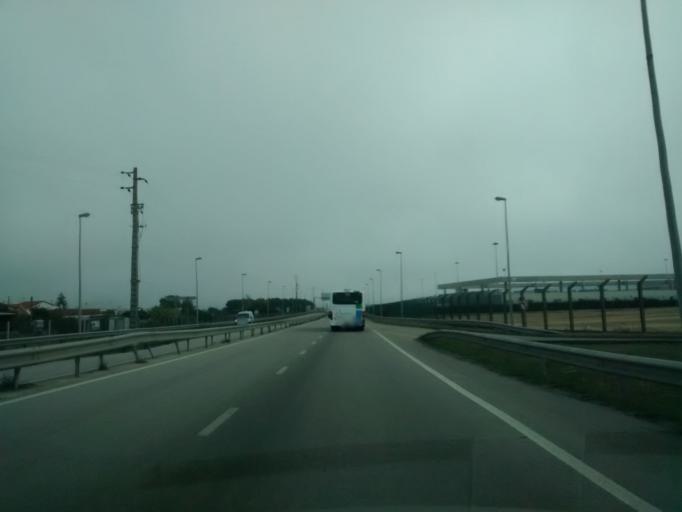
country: PT
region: Aveiro
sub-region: Ilhavo
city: Gafanha da Nazare
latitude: 40.6392
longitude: -8.7265
